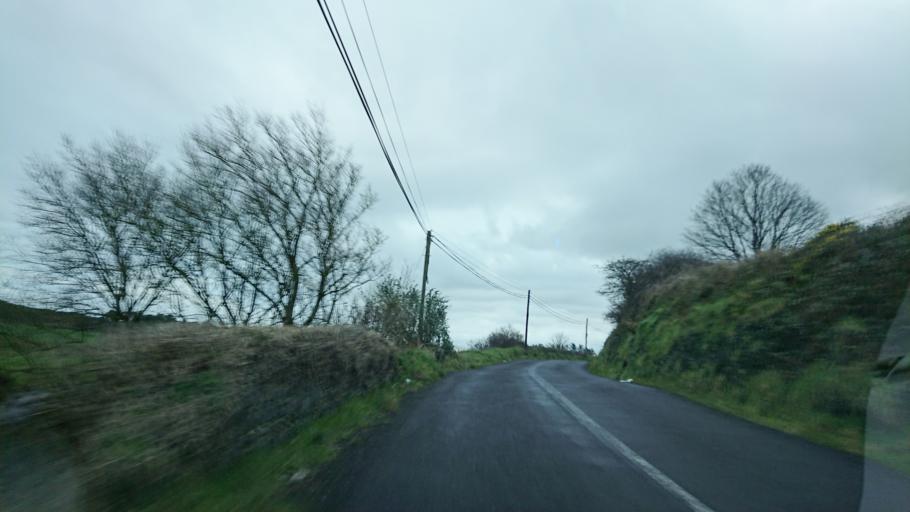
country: IE
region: Munster
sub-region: Waterford
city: Portlaw
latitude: 52.1445
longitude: -7.3757
